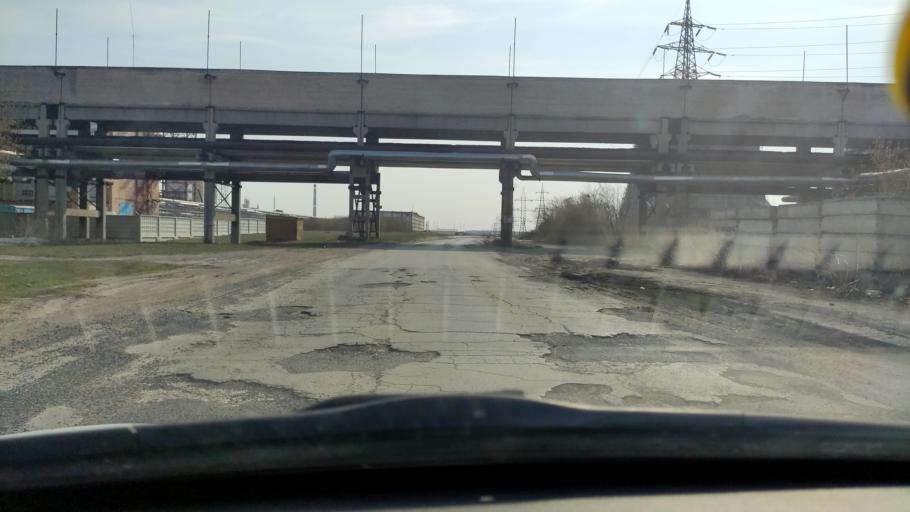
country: RU
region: Samara
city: Tol'yatti
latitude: 53.5500
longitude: 49.4561
